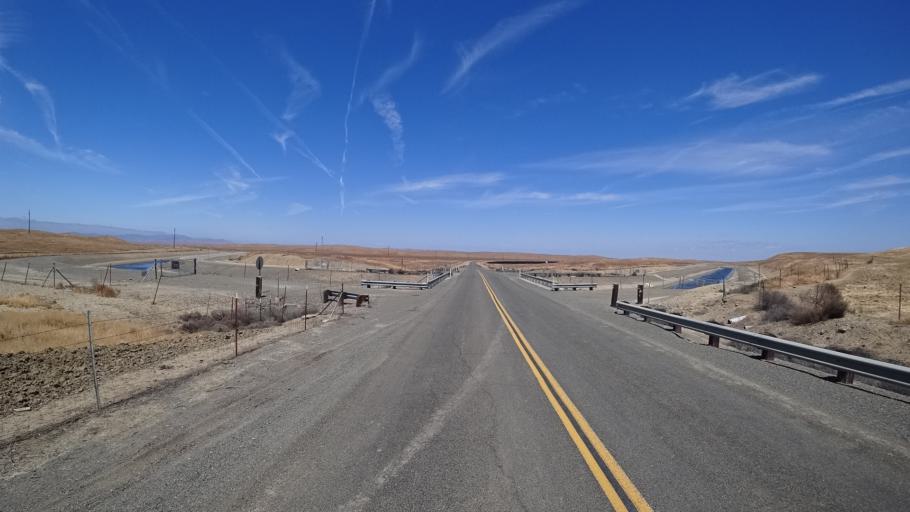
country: US
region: California
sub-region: Kings County
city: Kettleman City
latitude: 35.8291
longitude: -119.9124
